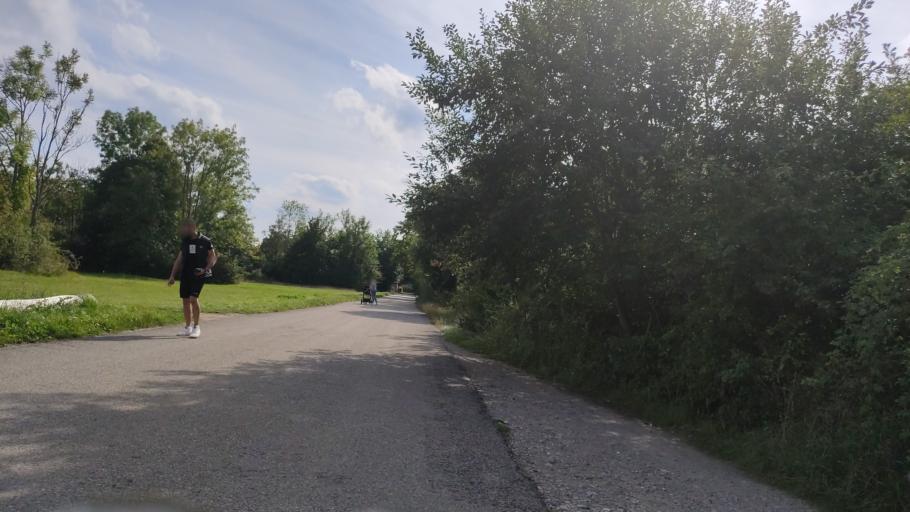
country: DE
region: Bavaria
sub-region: Swabia
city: Klosterlechfeld
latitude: 48.1644
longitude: 10.8384
